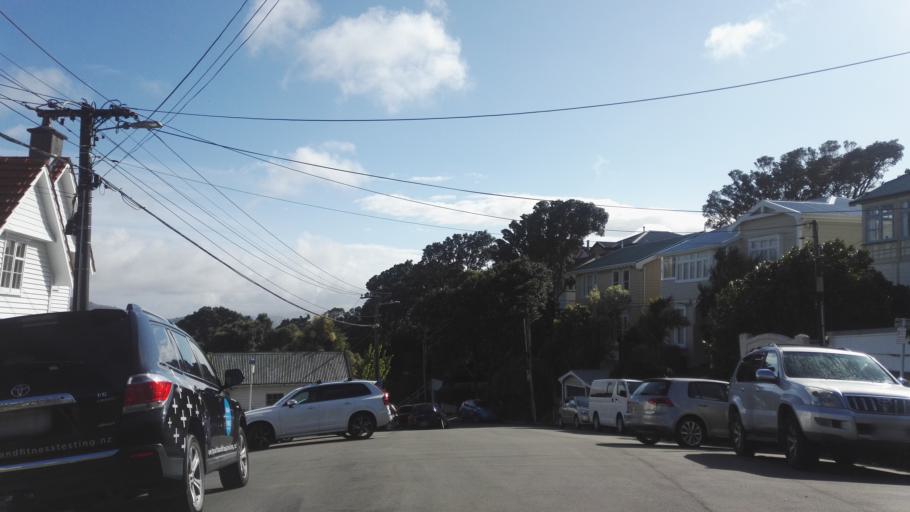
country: NZ
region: Wellington
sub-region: Wellington City
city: Kelburn
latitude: -41.2898
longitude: 174.7641
